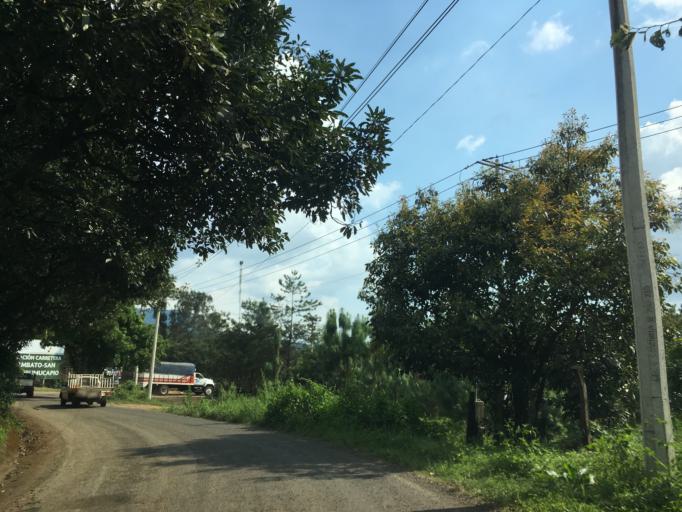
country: MX
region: Michoacan
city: Tingambato
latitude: 19.4623
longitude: -101.8656
